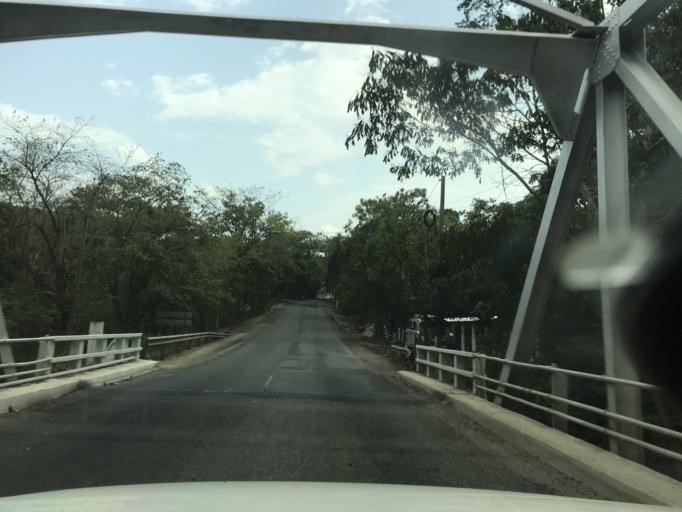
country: GT
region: Zacapa
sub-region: Municipio de Zacapa
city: Gualan
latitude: 15.1801
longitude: -89.3026
